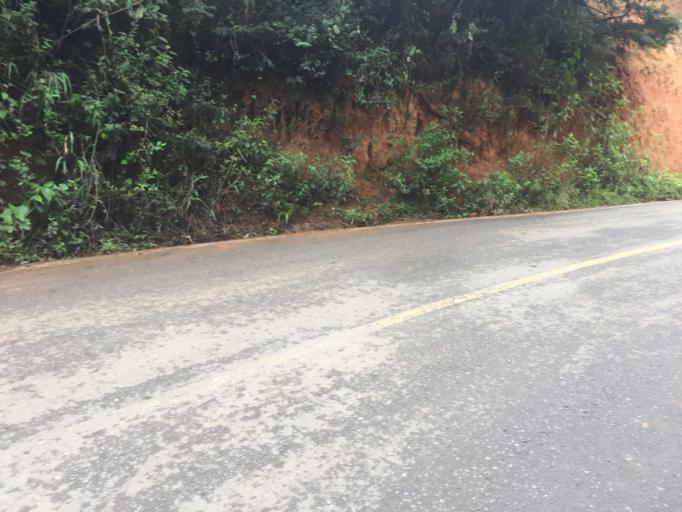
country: CO
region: Valle del Cauca
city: Dagua
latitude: 3.6889
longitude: -76.5935
